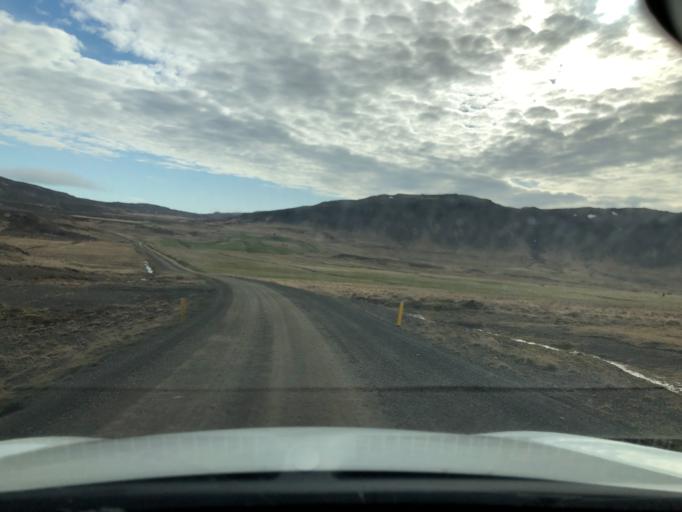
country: IS
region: West
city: Stykkisholmur
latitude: 65.0148
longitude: -22.5647
